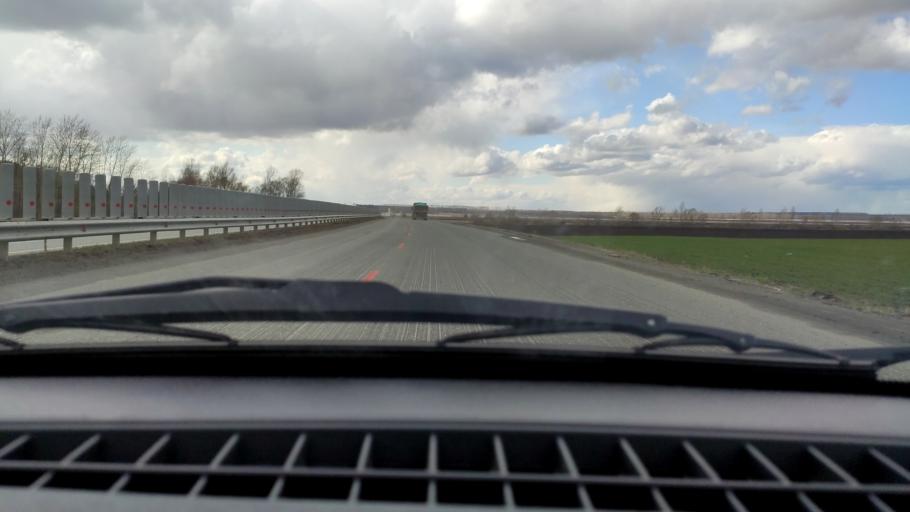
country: RU
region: Bashkortostan
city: Kushnarenkovo
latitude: 55.0645
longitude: 55.3662
